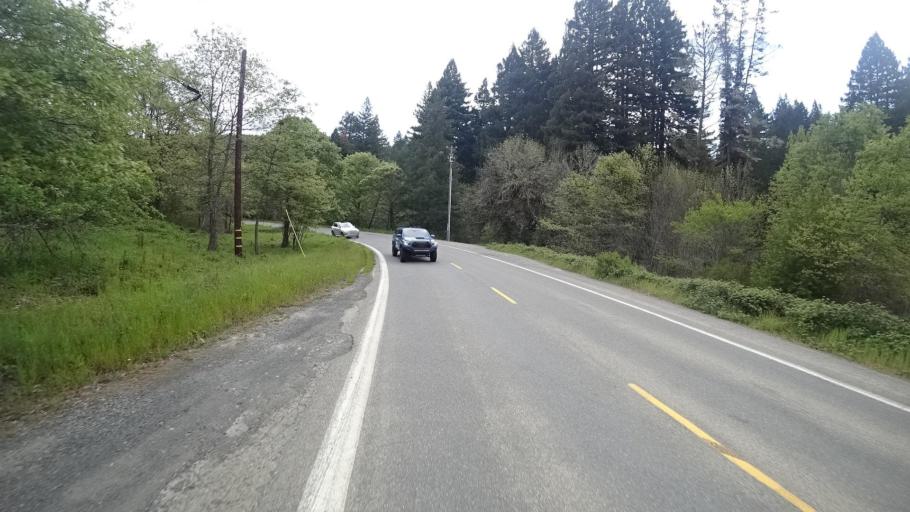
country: US
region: California
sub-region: Humboldt County
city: Redway
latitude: 40.1105
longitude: -123.8922
